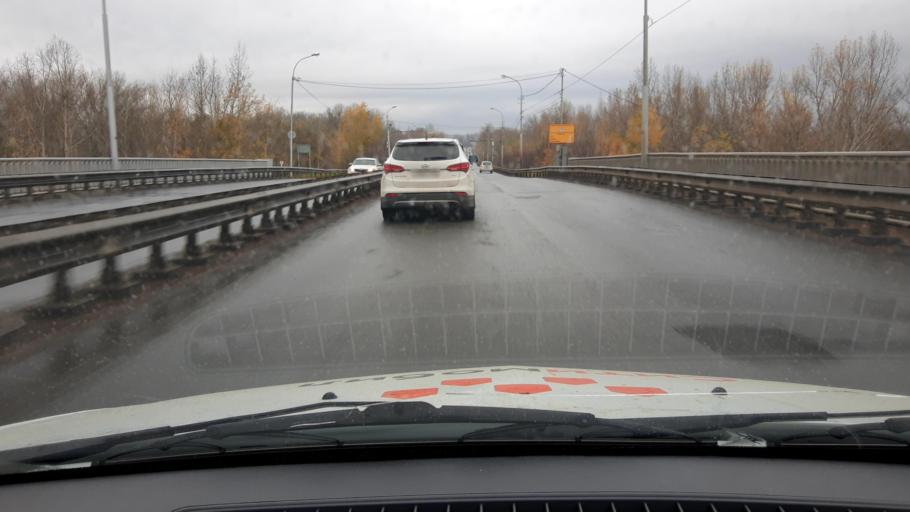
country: RU
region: Bashkortostan
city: Iglino
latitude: 54.7884
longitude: 56.2169
